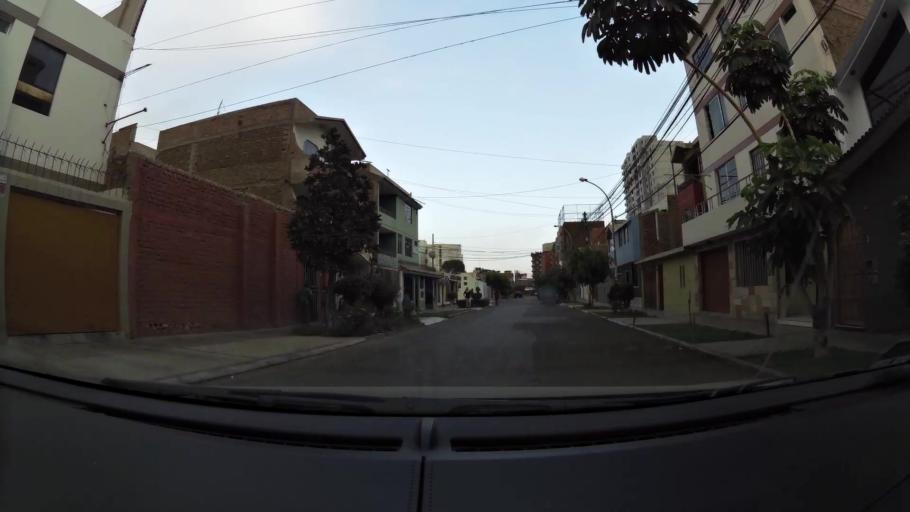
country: PE
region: La Libertad
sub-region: Provincia de Trujillo
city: Trujillo
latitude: -8.0961
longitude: -79.0253
